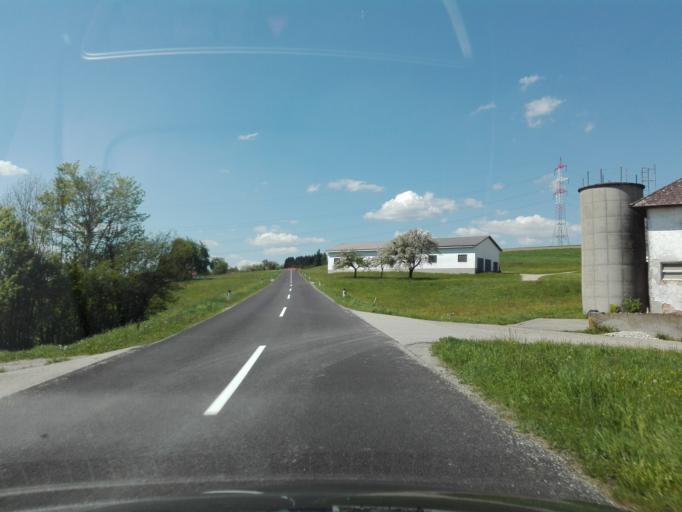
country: AT
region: Upper Austria
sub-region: Politischer Bezirk Rohrbach
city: Kleinzell im Muehlkreis
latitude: 48.3601
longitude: 13.9363
